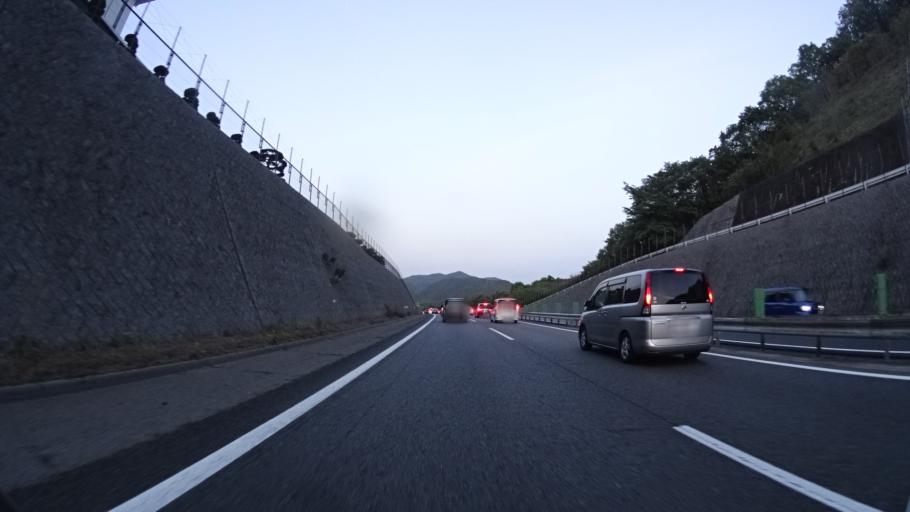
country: JP
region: Hyogo
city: Kariya
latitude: 34.7787
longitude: 134.2349
